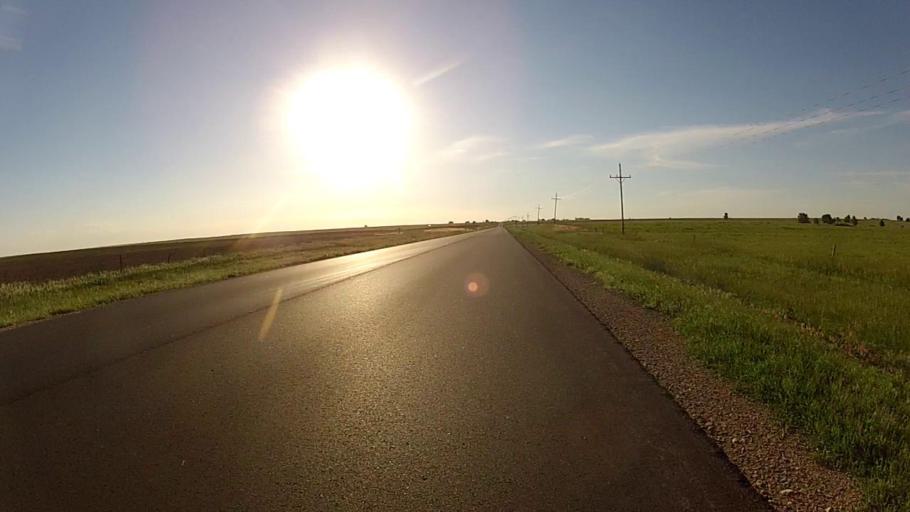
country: US
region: Kansas
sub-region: Comanche County
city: Coldwater
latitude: 37.2814
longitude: -99.1905
